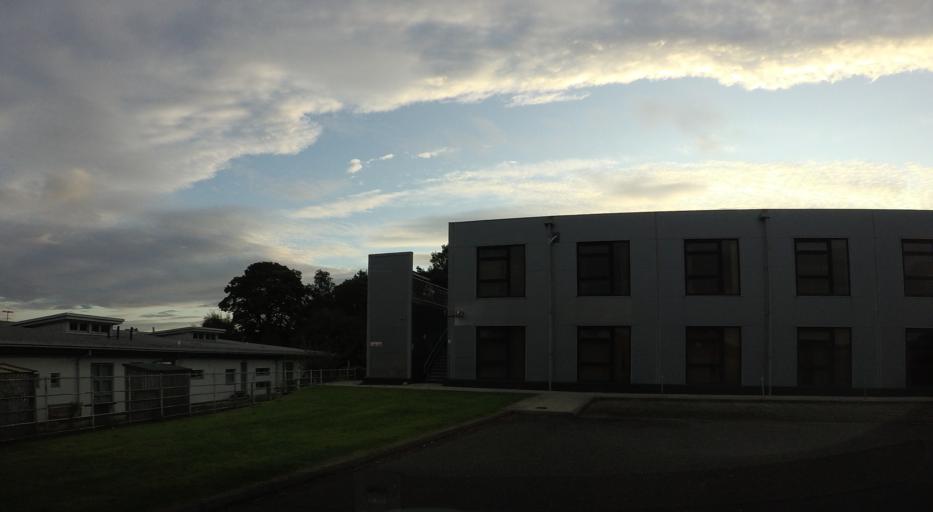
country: GB
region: Scotland
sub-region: West Lothian
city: West Calder
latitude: 55.8728
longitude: -3.5494
